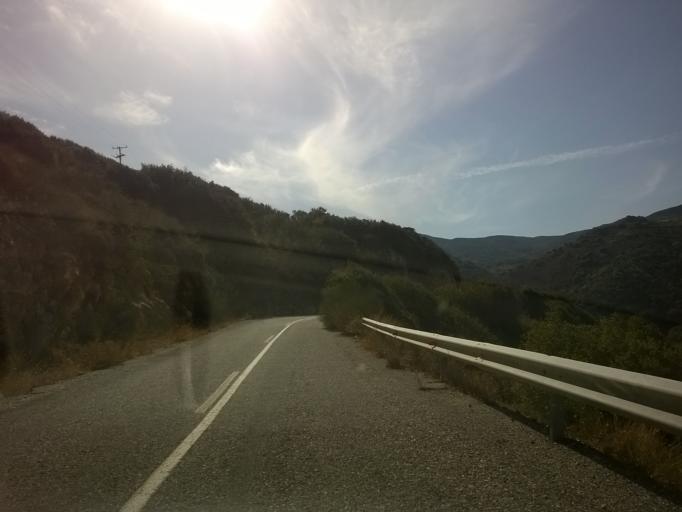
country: GR
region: South Aegean
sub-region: Nomos Kykladon
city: Filotion
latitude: 37.1483
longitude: 25.5476
